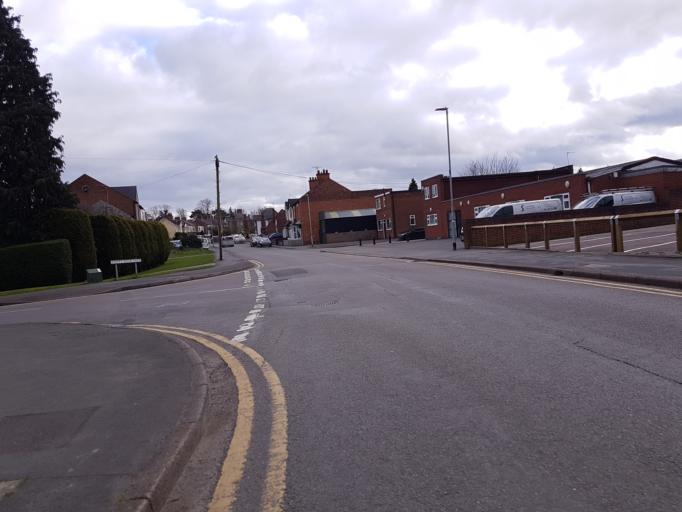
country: GB
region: England
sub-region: Leicestershire
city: Earl Shilton
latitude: 52.5742
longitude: -1.3166
